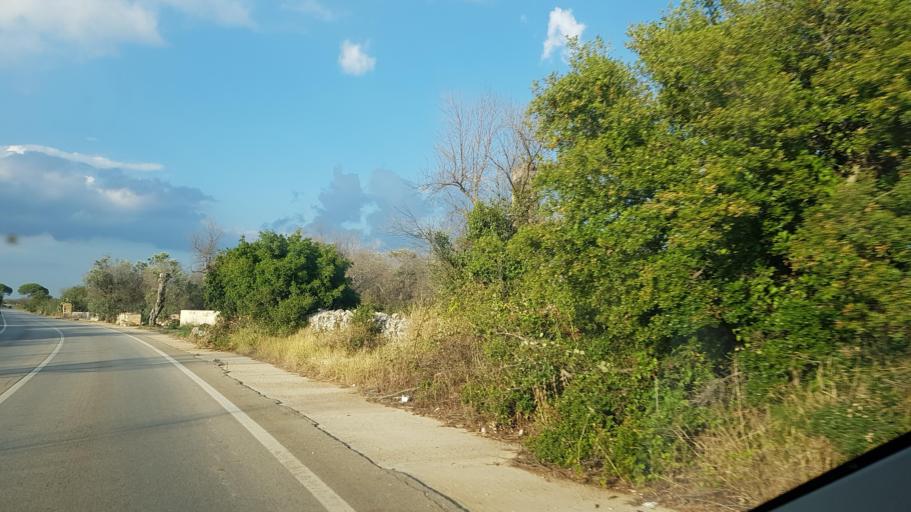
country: IT
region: Apulia
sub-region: Provincia di Lecce
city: Acquarica del Capo
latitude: 39.8806
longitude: 18.2322
